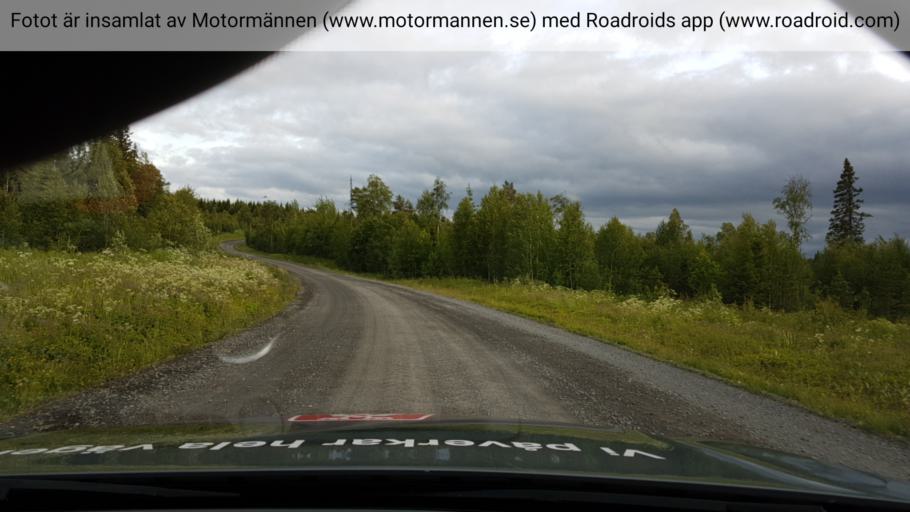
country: SE
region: Jaemtland
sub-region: OEstersunds Kommun
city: Lit
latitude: 63.5838
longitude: 14.9808
